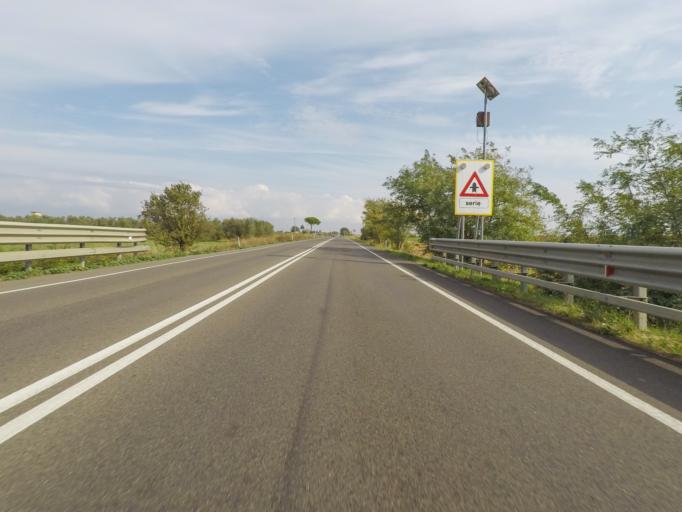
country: IT
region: Tuscany
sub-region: Provincia di Grosseto
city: Capalbio
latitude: 42.4146
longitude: 11.4196
